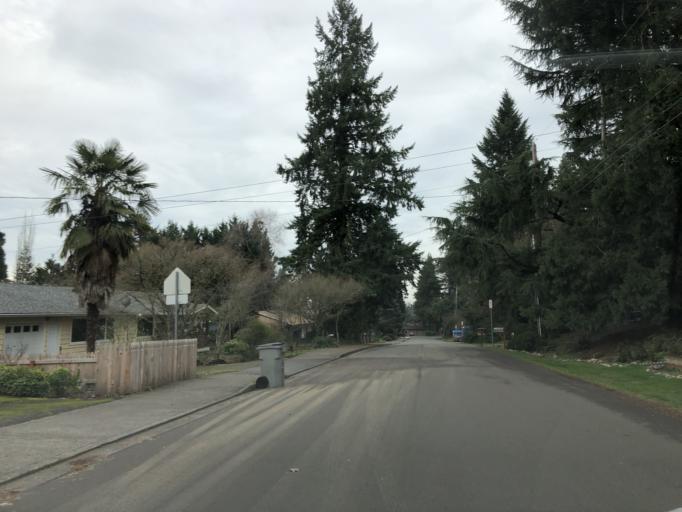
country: US
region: Oregon
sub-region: Washington County
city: Tigard
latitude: 45.4120
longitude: -122.7754
